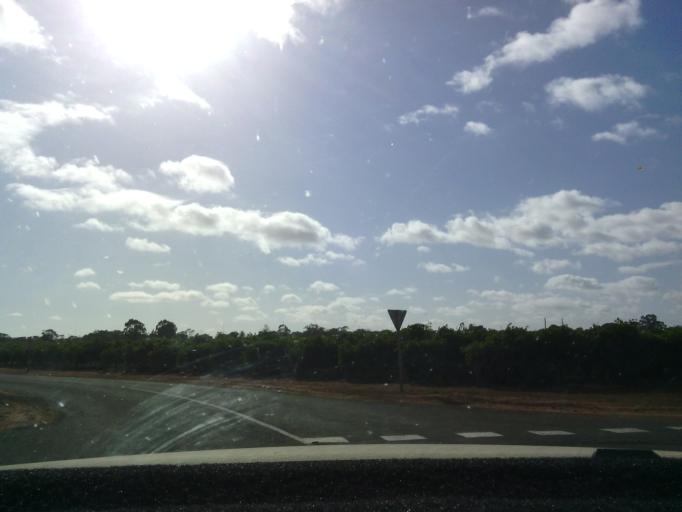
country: AU
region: South Australia
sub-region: Berri and Barmera
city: Monash
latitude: -34.2351
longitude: 140.5644
